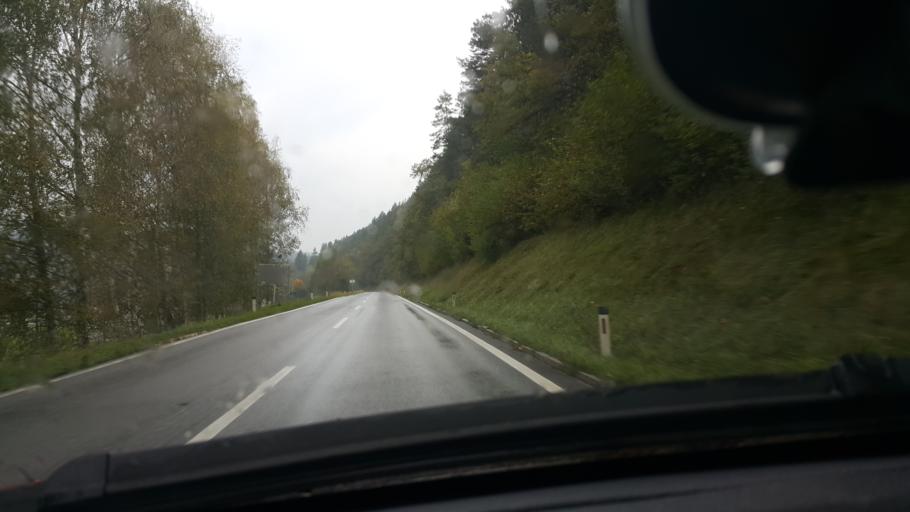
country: AT
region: Carinthia
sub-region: Politischer Bezirk Wolfsberg
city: Lavamund
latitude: 46.6463
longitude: 14.9362
